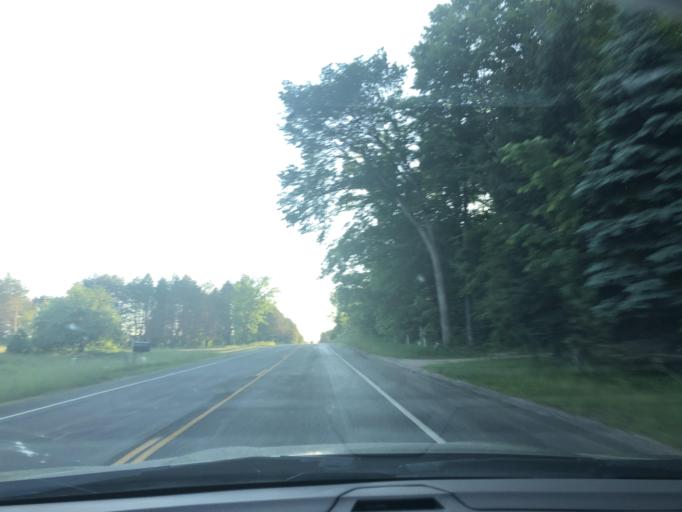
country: US
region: Michigan
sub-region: Missaukee County
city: Lake City
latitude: 44.4673
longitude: -85.1374
